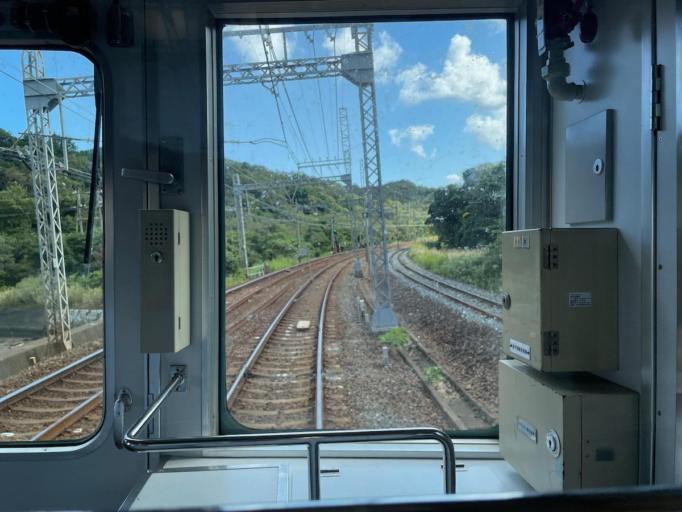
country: JP
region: Mie
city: Toba
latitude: 34.4868
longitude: 136.8282
